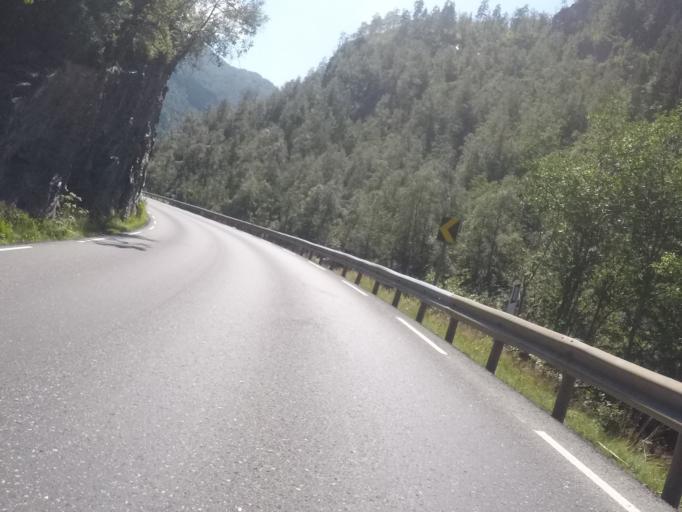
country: NO
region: Hordaland
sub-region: Voss
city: Voss
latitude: 60.7597
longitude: 6.4908
